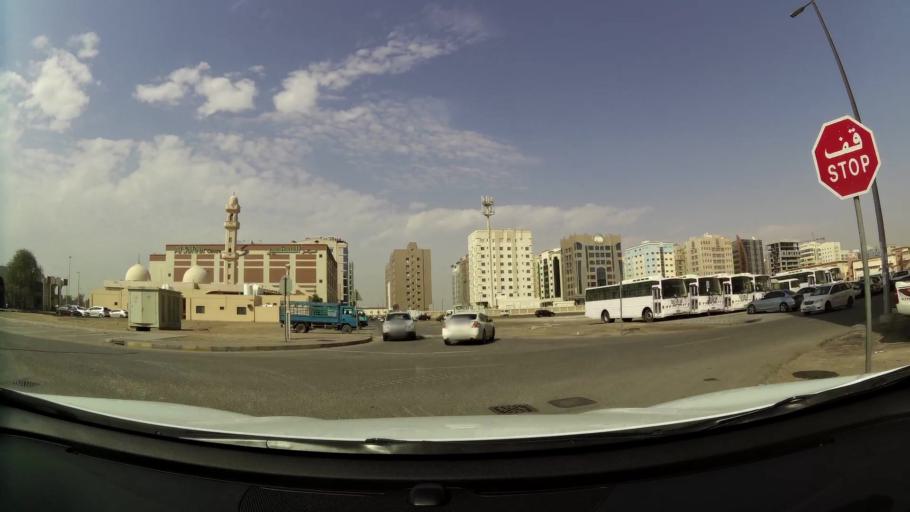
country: AE
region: Abu Dhabi
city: Abu Dhabi
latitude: 24.3416
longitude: 54.5309
